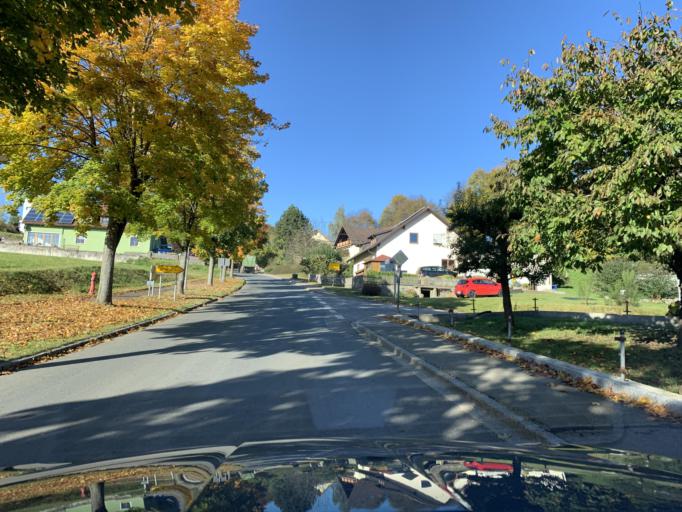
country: DE
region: Bavaria
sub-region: Upper Palatinate
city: Thanstein
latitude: 49.3792
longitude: 12.4744
